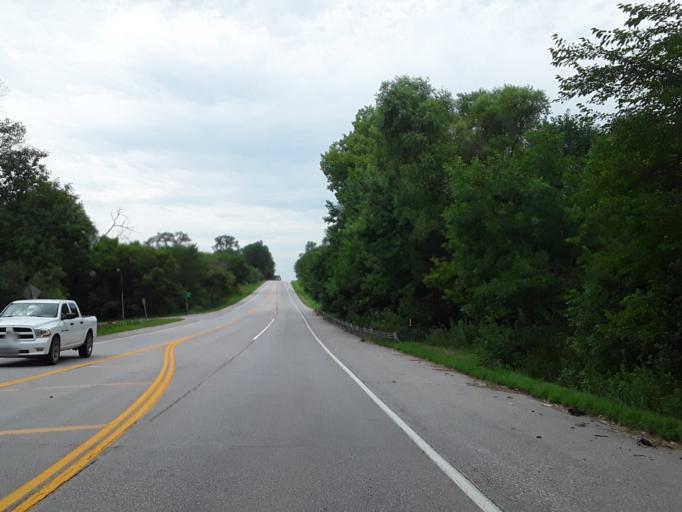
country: US
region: Nebraska
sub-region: Douglas County
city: Bennington
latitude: 41.3648
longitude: -96.0292
